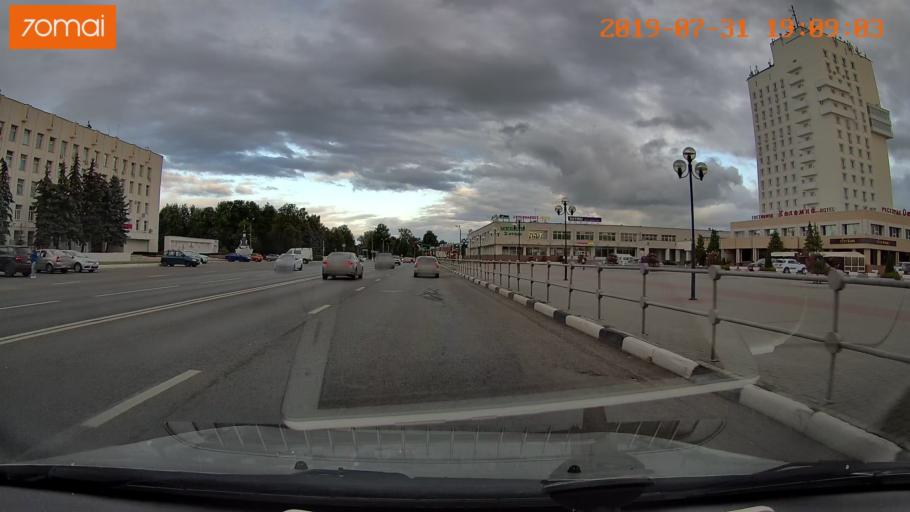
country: RU
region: Moskovskaya
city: Kolomna
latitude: 55.0956
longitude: 38.7653
